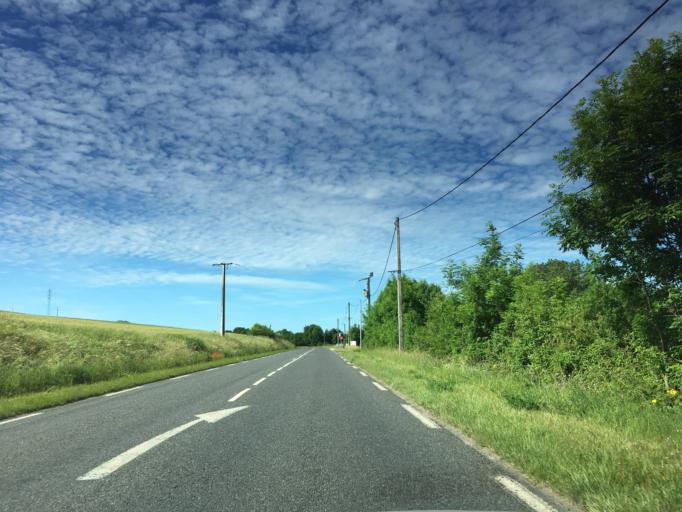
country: FR
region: Bourgogne
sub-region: Departement de l'Yonne
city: Auxerre
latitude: 47.7691
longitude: 3.5527
